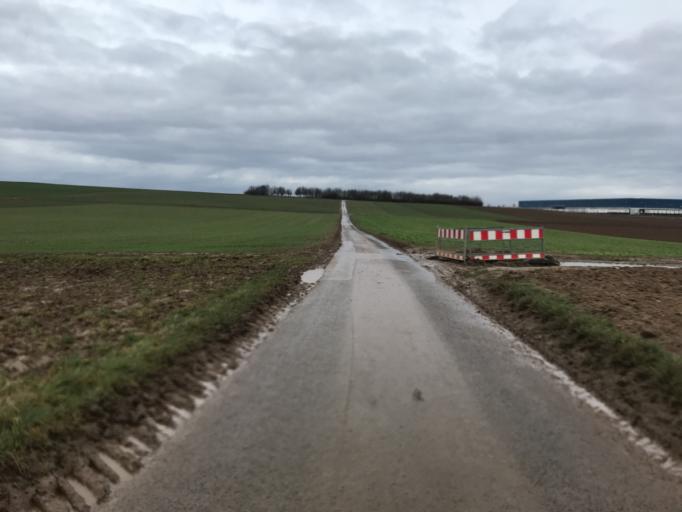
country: DE
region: Rheinland-Pfalz
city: Gau-Bischofsheim
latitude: 49.9350
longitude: 8.2500
